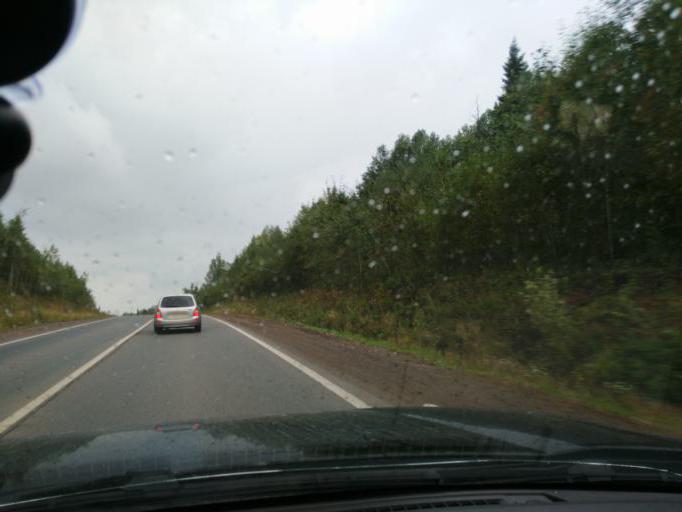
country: RU
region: Perm
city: Barda
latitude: 56.8917
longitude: 55.7723
